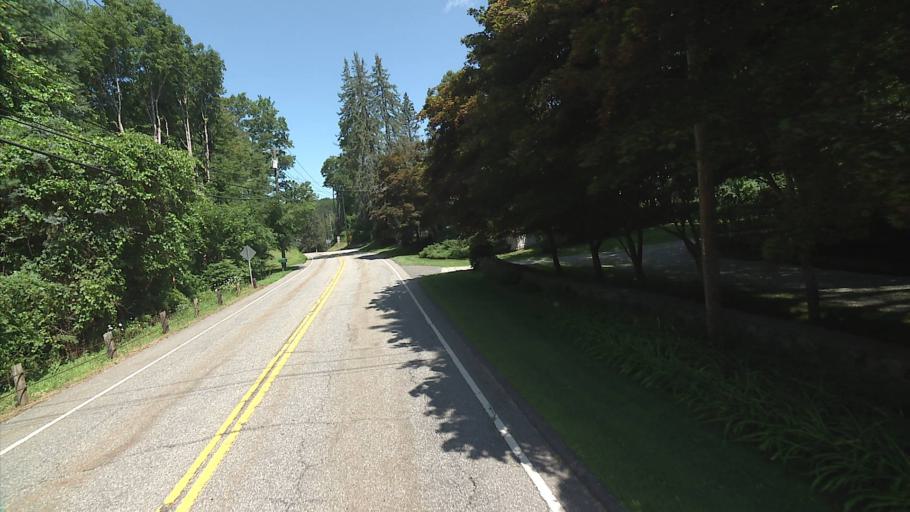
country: US
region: Connecticut
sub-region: Litchfield County
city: New Preston
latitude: 41.7015
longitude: -73.3449
